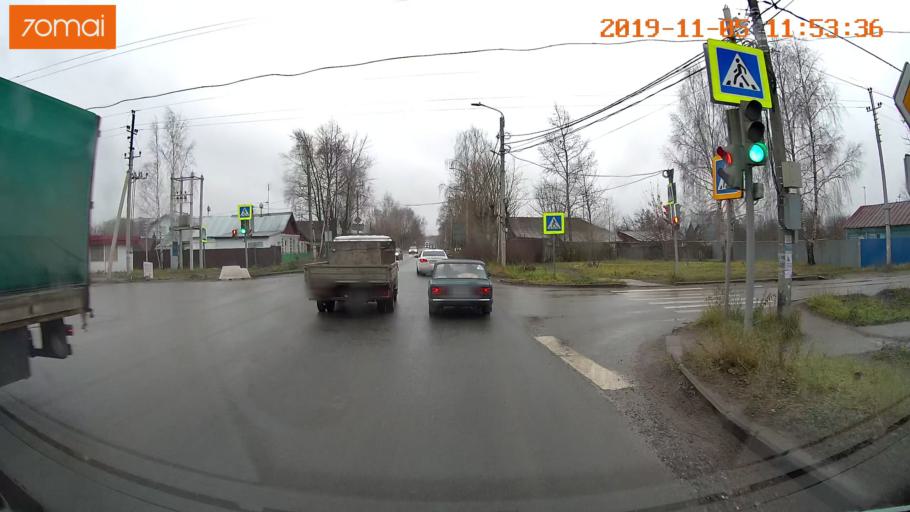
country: RU
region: Ivanovo
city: Bogorodskoye
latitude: 56.9953
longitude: 41.0304
